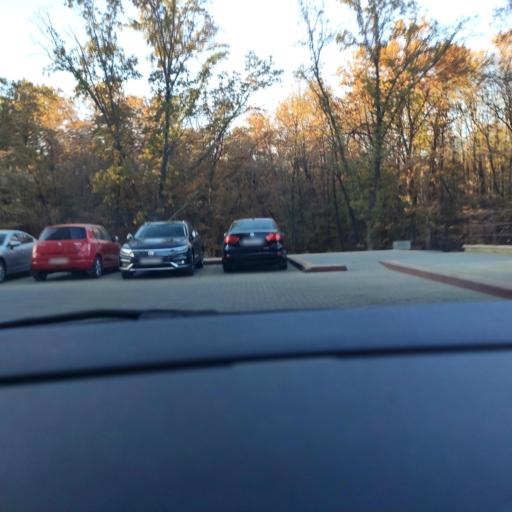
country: RU
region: Voronezj
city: Voronezh
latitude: 51.7168
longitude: 39.1969
